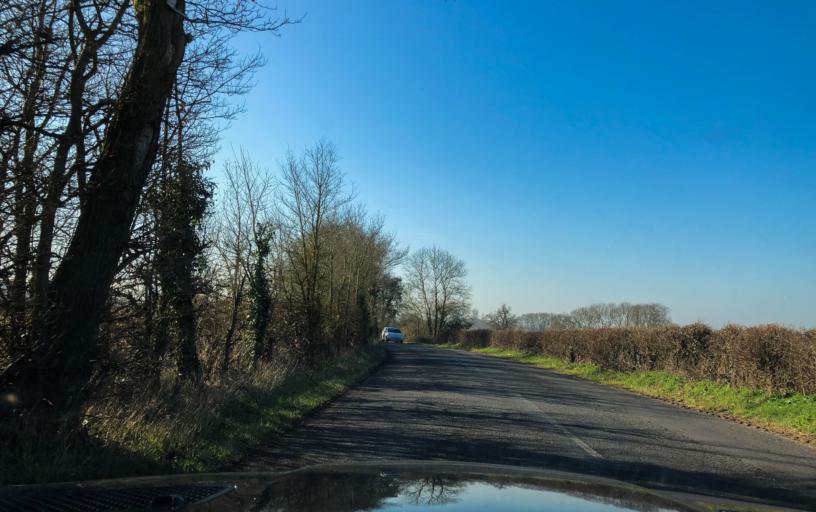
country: GB
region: England
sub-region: Warwickshire
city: Wellesbourne Mountford
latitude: 52.2292
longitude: -1.5619
